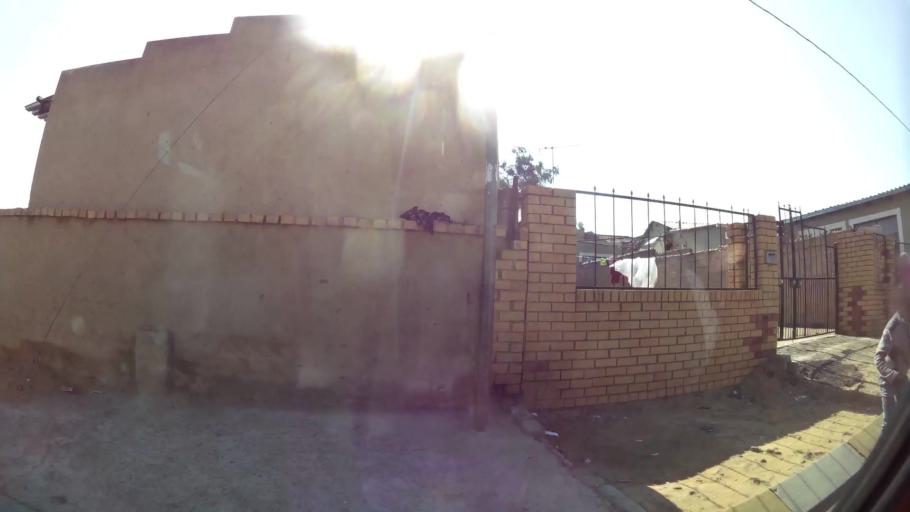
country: ZA
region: Gauteng
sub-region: City of Johannesburg Metropolitan Municipality
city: Soweto
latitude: -26.2505
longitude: 27.9399
